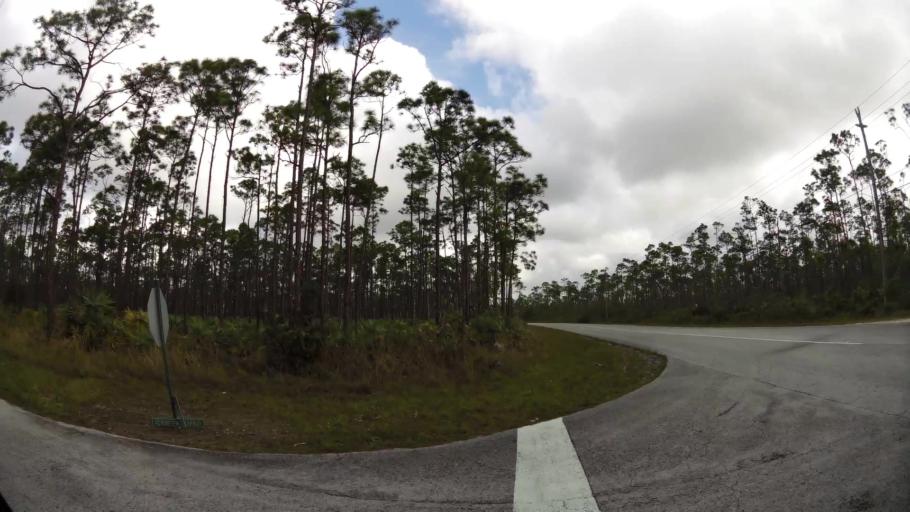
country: BS
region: Freeport
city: Lucaya
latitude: 26.5887
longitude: -78.5460
